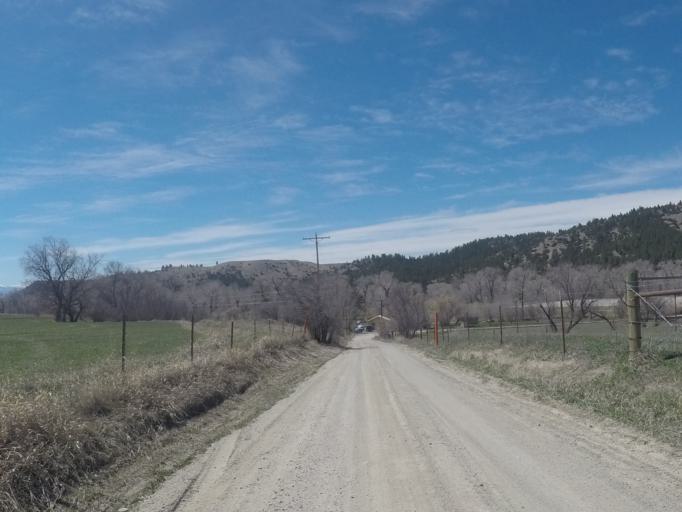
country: US
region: Montana
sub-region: Stillwater County
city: Columbus
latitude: 45.5803
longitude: -109.3271
